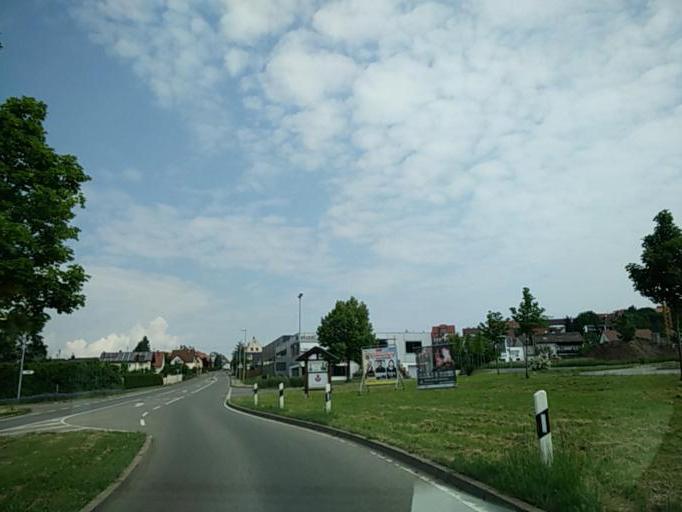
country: DE
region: Baden-Wuerttemberg
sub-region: Tuebingen Region
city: Rottenburg
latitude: 48.4460
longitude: 8.9203
